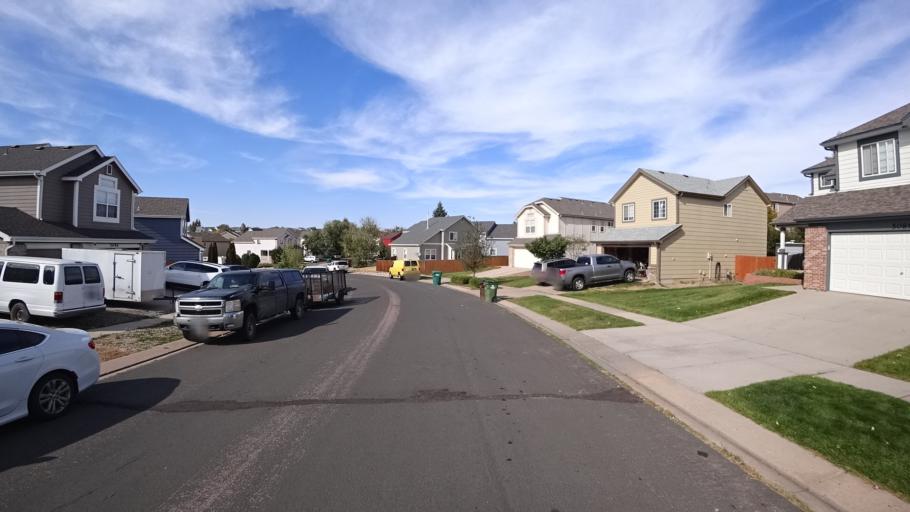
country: US
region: Colorado
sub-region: El Paso County
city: Cimarron Hills
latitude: 38.9067
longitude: -104.6929
